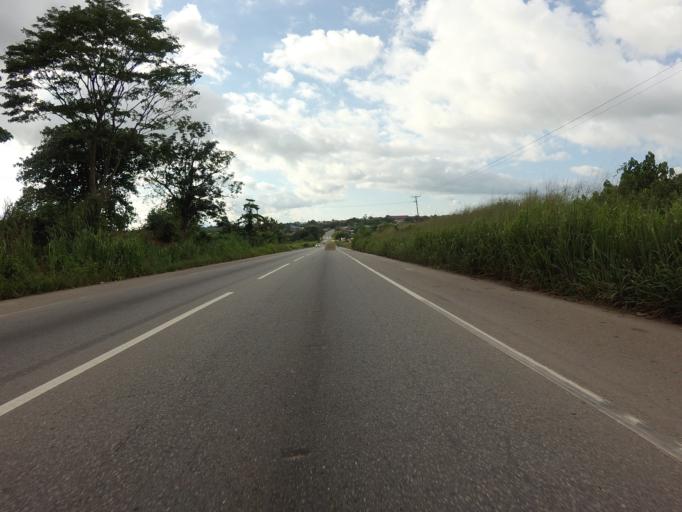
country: GH
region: Ashanti
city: Tafo
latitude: 6.8283
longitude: -1.6485
